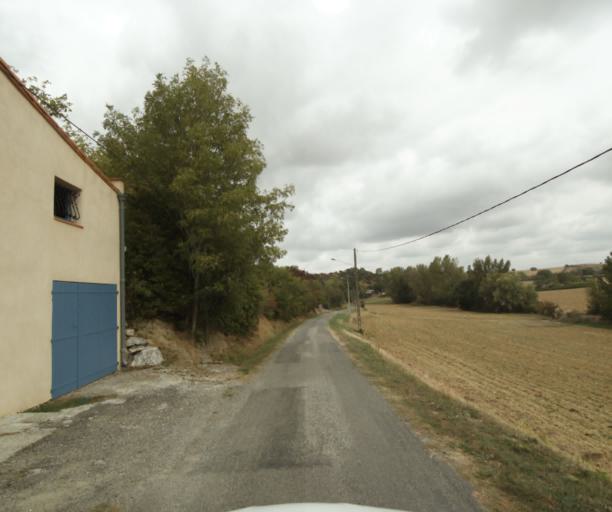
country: FR
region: Midi-Pyrenees
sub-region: Departement de la Haute-Garonne
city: Villefranche-de-Lauragais
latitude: 43.4081
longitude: 1.7173
